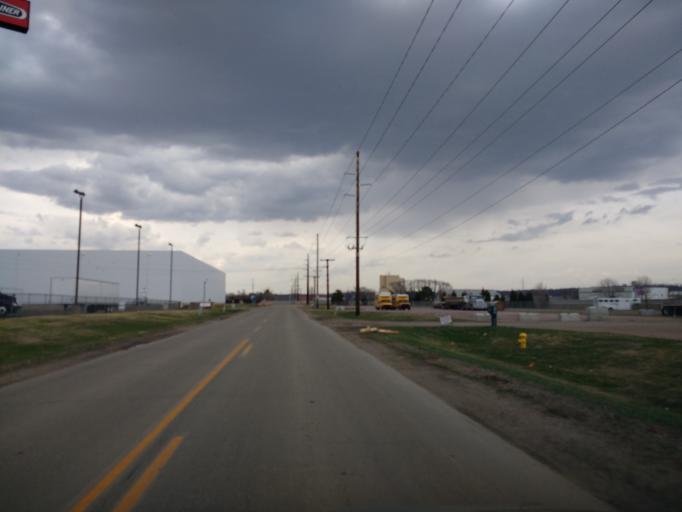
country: US
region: Iowa
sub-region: Woodbury County
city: Sergeant Bluff
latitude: 42.4235
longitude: -96.3698
